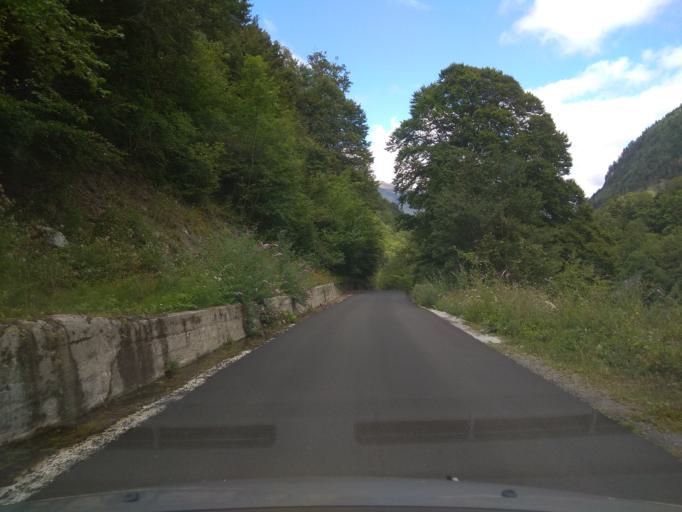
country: ES
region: Catalonia
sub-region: Provincia de Lleida
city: Vielha
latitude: 42.7033
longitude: 0.7119
